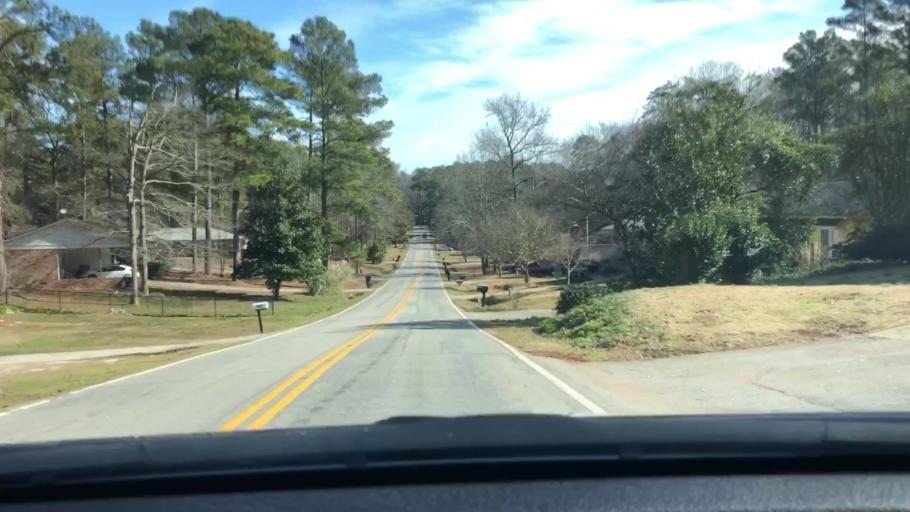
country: US
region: South Carolina
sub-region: Lexington County
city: Irmo
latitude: 34.0623
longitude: -81.1778
